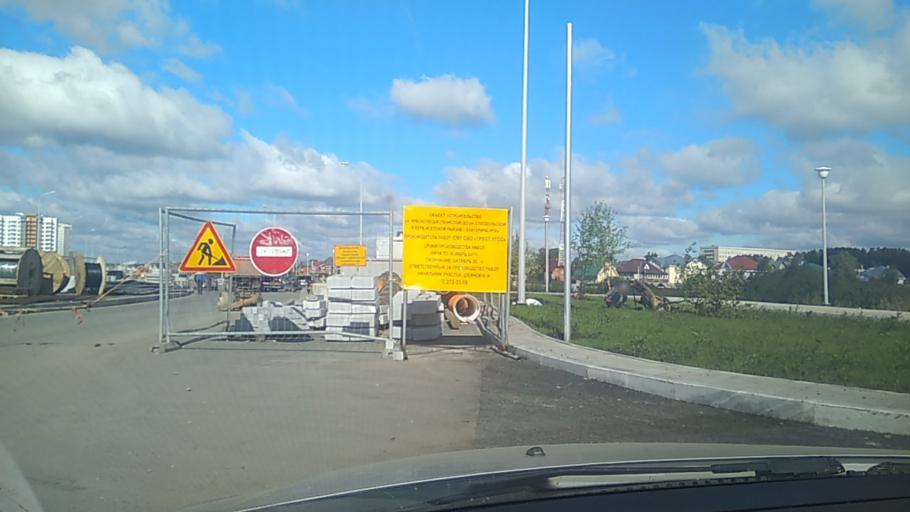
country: RU
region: Sverdlovsk
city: Shirokaya Rechka
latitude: 56.7992
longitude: 60.5109
